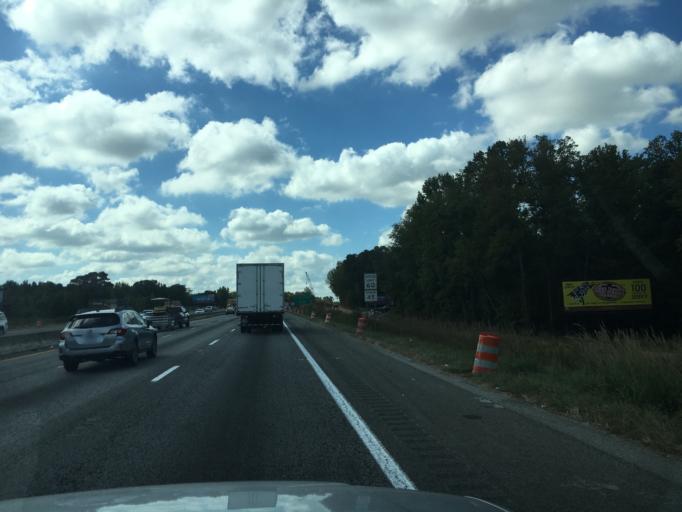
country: US
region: South Carolina
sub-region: Greenville County
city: Five Forks
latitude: 34.8459
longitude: -82.2811
